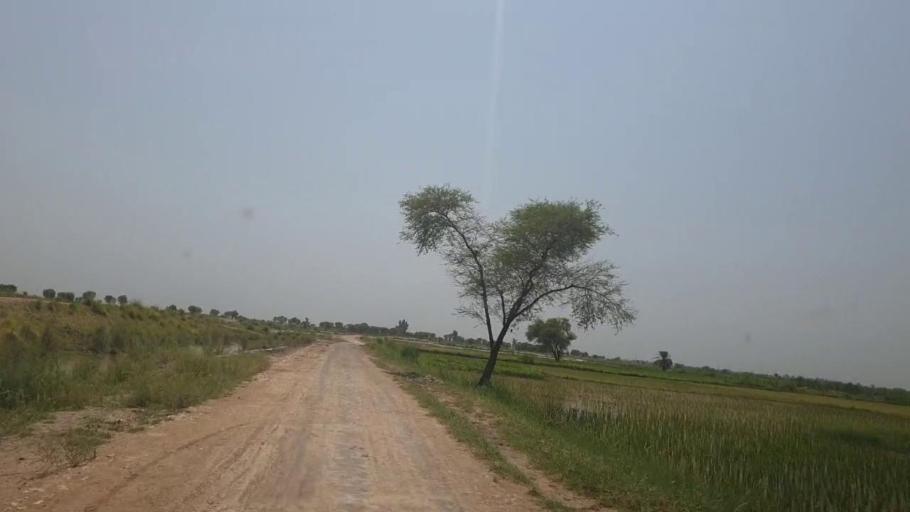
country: PK
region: Sindh
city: Lakhi
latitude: 27.8550
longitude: 68.6651
